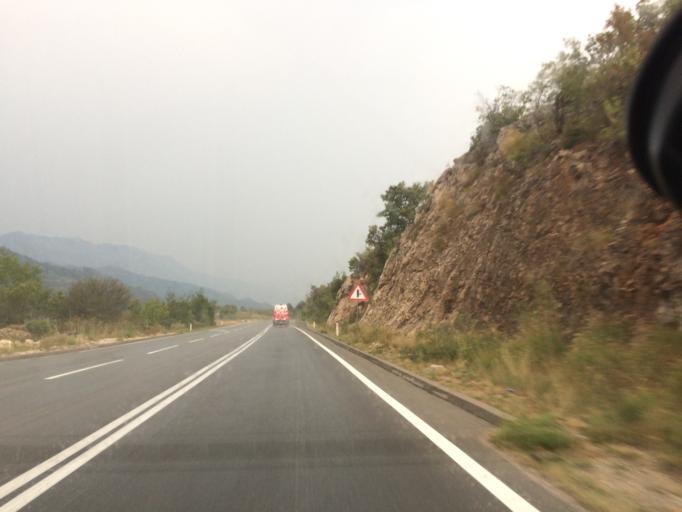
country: ME
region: Opstina Niksic
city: Niksic
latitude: 42.7162
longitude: 18.9469
